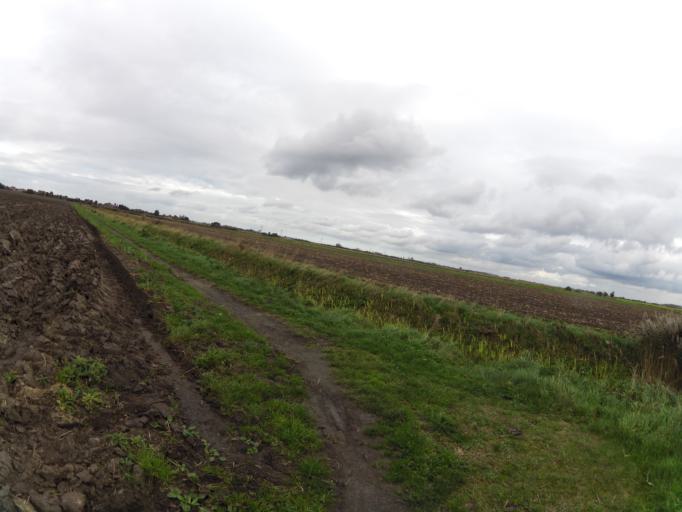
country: BE
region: Flanders
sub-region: Provincie West-Vlaanderen
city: Gistel
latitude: 51.1292
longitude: 2.9302
